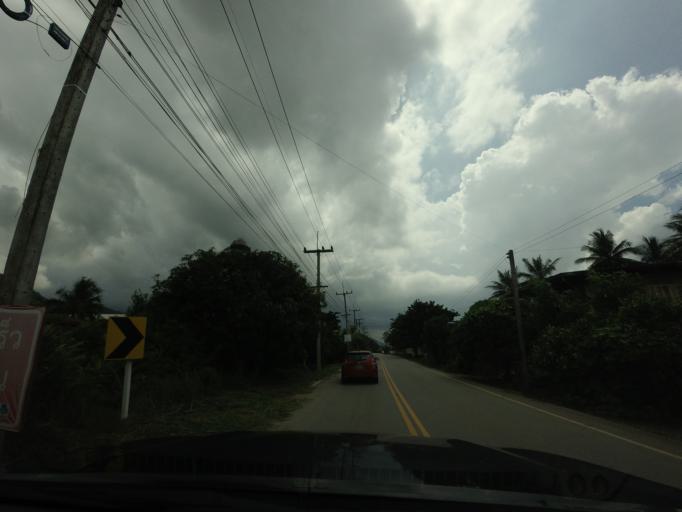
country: LA
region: Vientiane
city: Muang Sanakham
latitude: 18.0042
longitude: 101.7571
